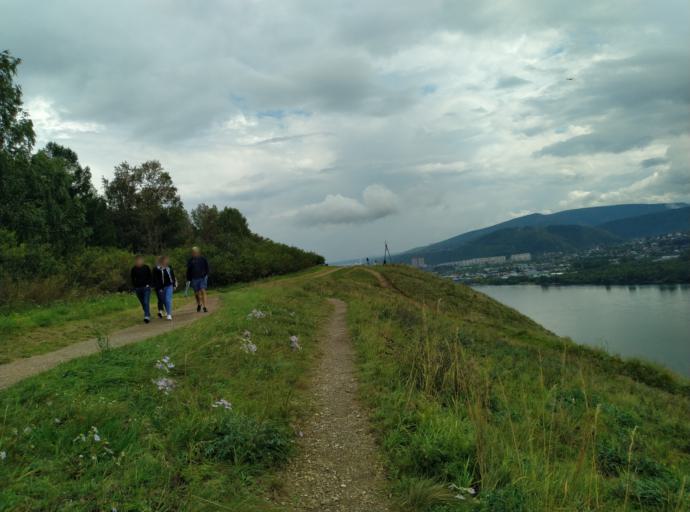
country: RU
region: Krasnoyarskiy
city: Krasnoyarsk
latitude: 55.9831
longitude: 92.7497
